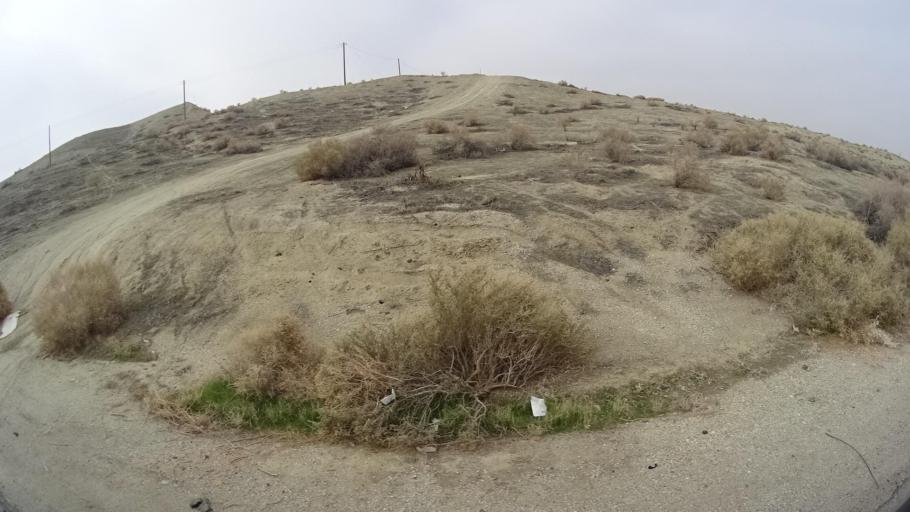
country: US
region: California
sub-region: Kern County
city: Maricopa
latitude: 35.0819
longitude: -119.3979
